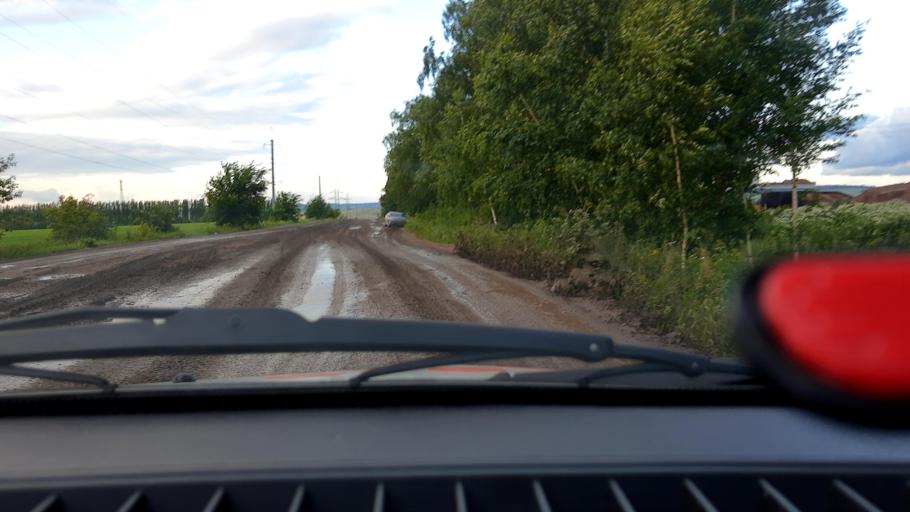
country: RU
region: Bashkortostan
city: Tolbazy
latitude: 54.1937
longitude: 55.8825
